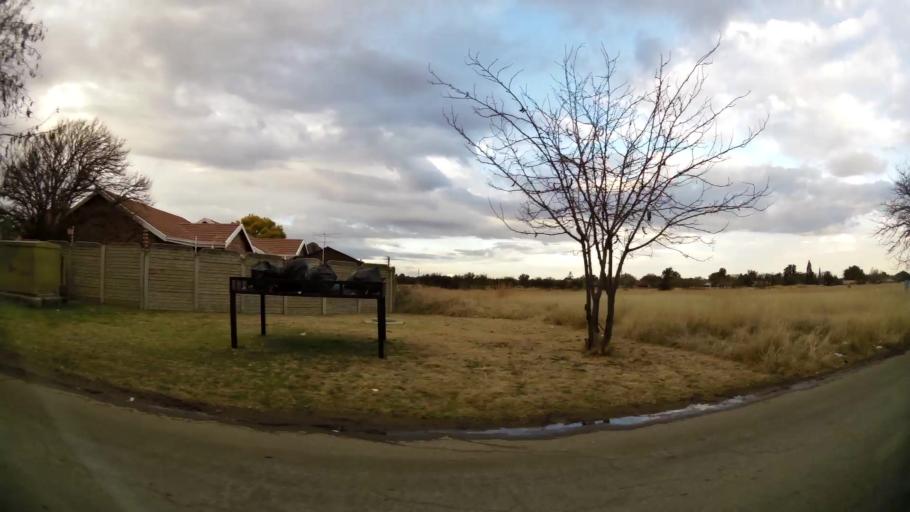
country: ZA
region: Orange Free State
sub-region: Lejweleputswa District Municipality
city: Welkom
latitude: -27.9762
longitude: 26.7001
